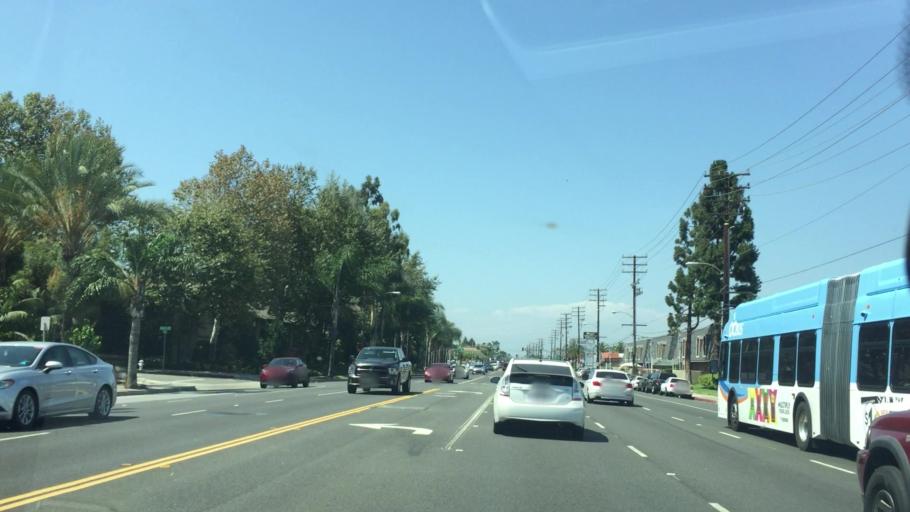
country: US
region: California
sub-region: Orange County
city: Santa Ana
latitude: 33.7049
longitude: -117.8855
